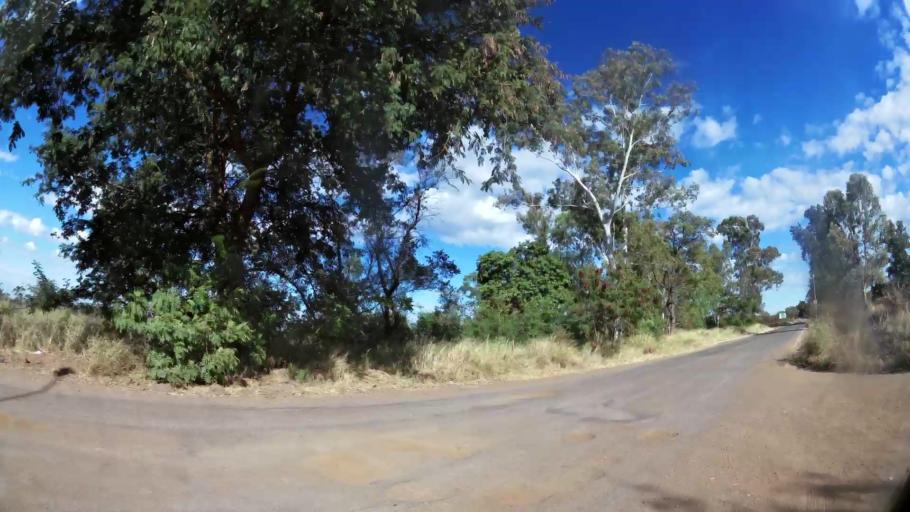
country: ZA
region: Limpopo
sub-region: Waterberg District Municipality
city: Warmbaths
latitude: -24.8812
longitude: 28.2748
